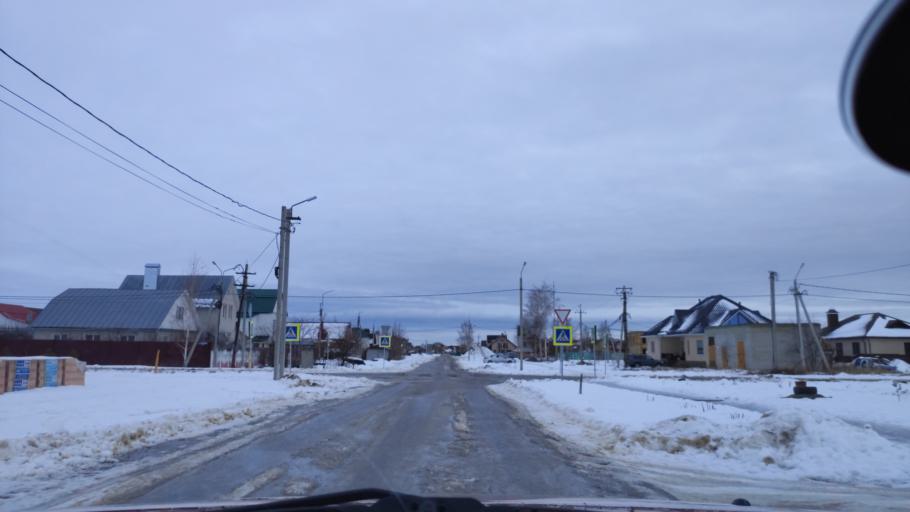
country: RU
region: Tambov
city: Tambov
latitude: 52.7665
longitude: 41.3706
